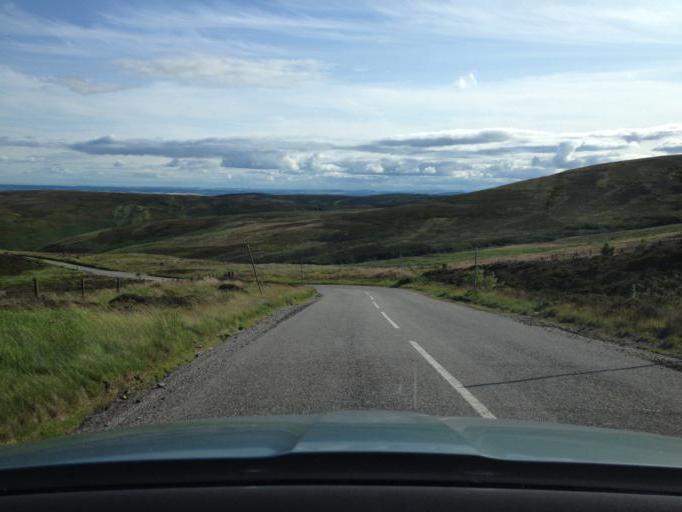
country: GB
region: Scotland
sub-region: Aberdeenshire
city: Laurencekirk
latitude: 56.9120
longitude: -2.5729
